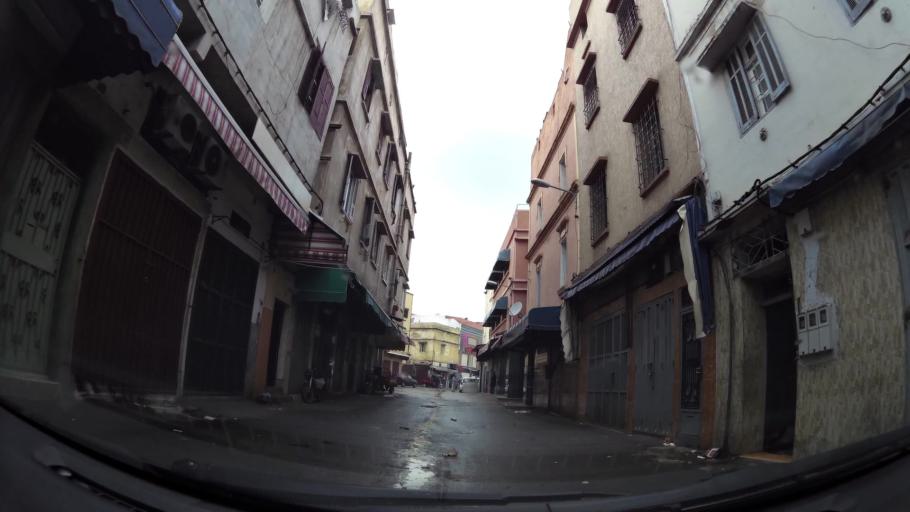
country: MA
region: Grand Casablanca
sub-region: Casablanca
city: Casablanca
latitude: 33.5762
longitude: -7.6019
